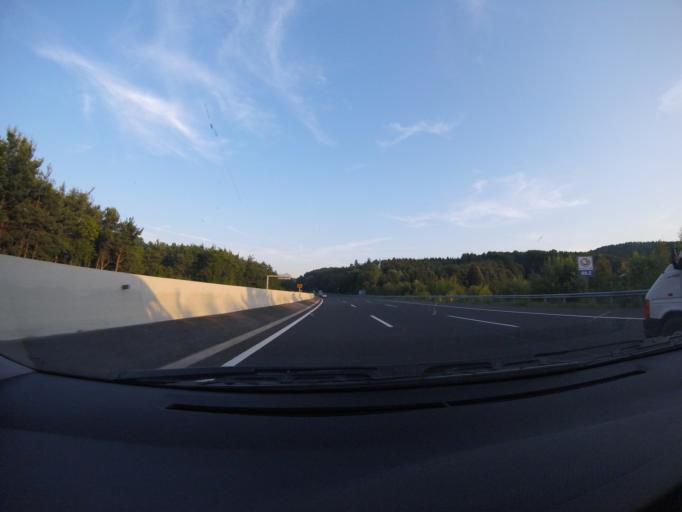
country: AT
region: Styria
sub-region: Politischer Bezirk Hartberg-Fuerstenfeld
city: Bad Waltersdorf
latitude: 47.1771
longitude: 15.9967
